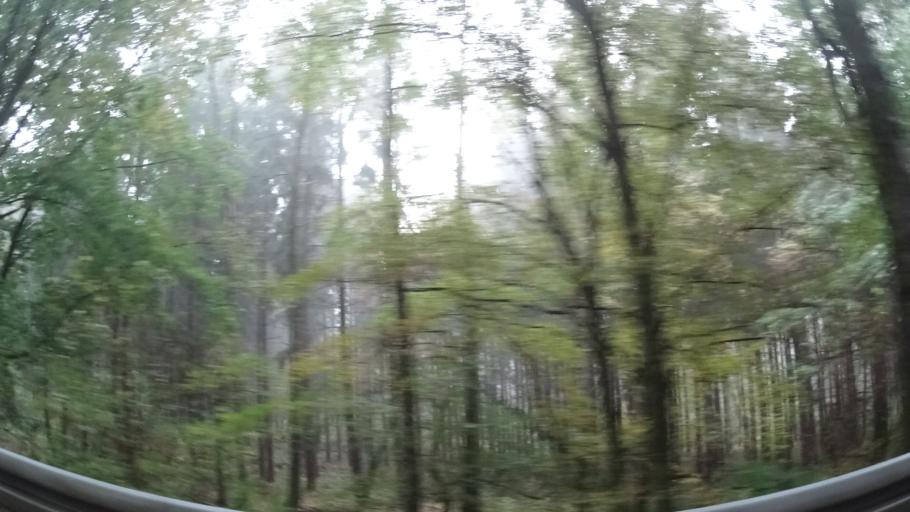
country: DE
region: Hesse
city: Gedern
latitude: 50.4440
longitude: 9.2163
